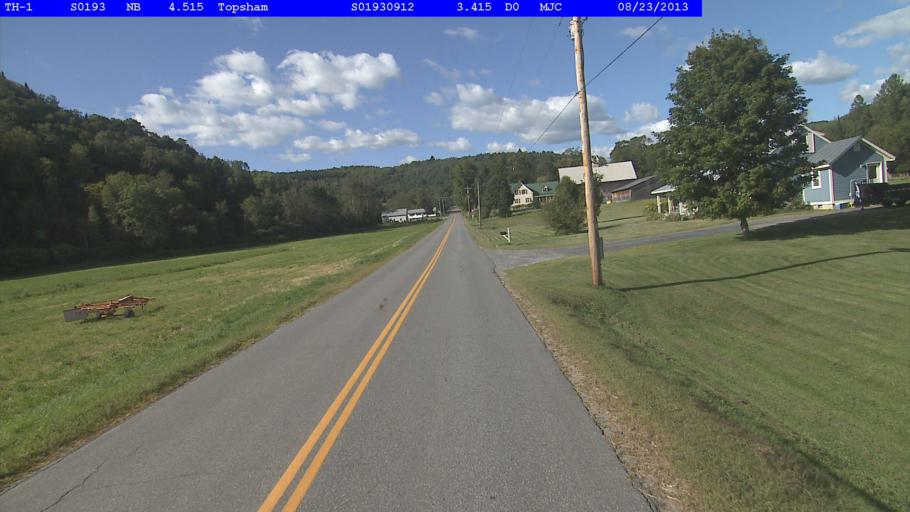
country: US
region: New Hampshire
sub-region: Grafton County
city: Haverhill
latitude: 44.1165
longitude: -72.2330
